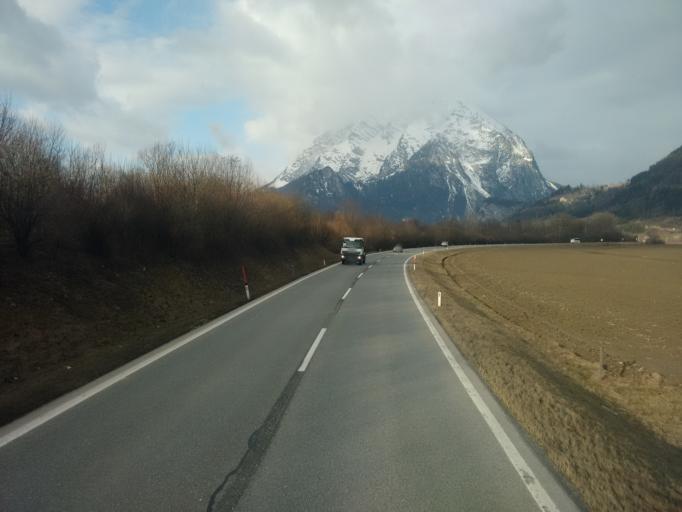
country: AT
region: Styria
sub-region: Politischer Bezirk Liezen
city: Stainach
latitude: 47.5248
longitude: 14.1050
